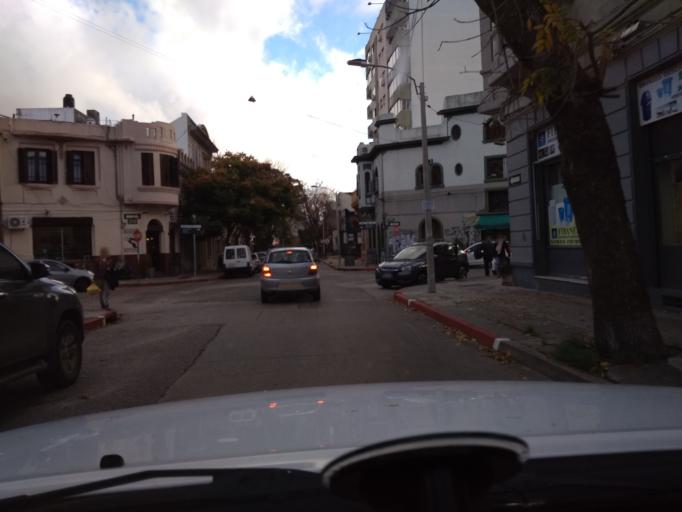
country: UY
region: Montevideo
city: Montevideo
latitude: -34.9112
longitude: -56.1589
